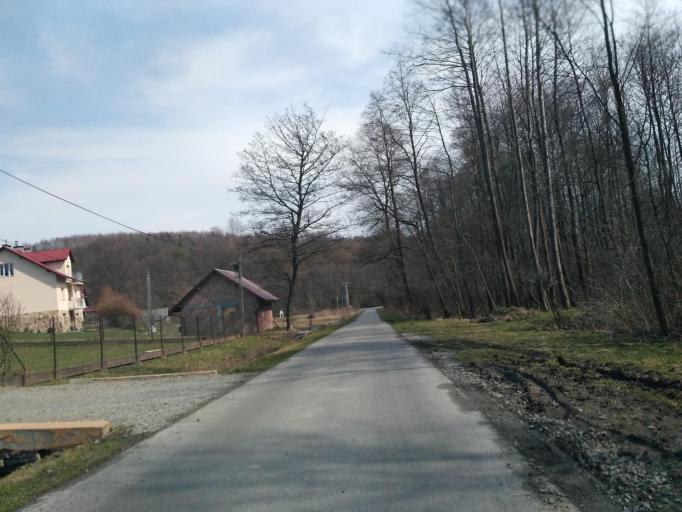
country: PL
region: Subcarpathian Voivodeship
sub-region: Powiat strzyzowski
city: Czudec
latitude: 49.9388
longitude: 21.7863
